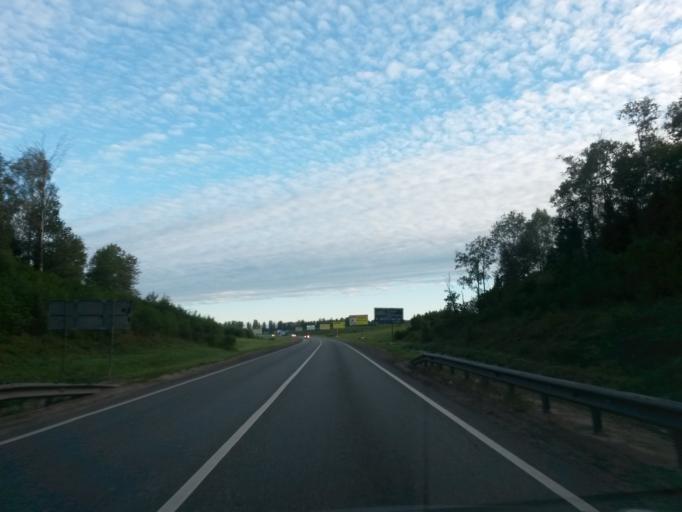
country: RU
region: Vladimir
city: Strunino
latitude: 56.5559
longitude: 38.5873
